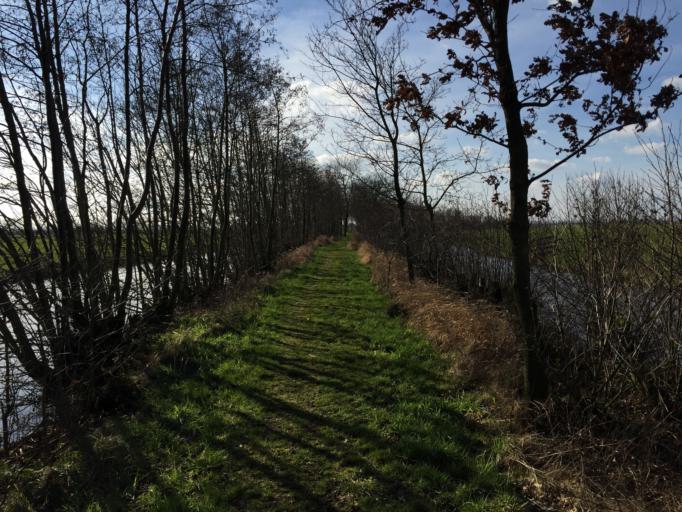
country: NL
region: Utrecht
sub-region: Gemeente Lopik
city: Lopik
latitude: 51.9885
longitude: 4.9355
